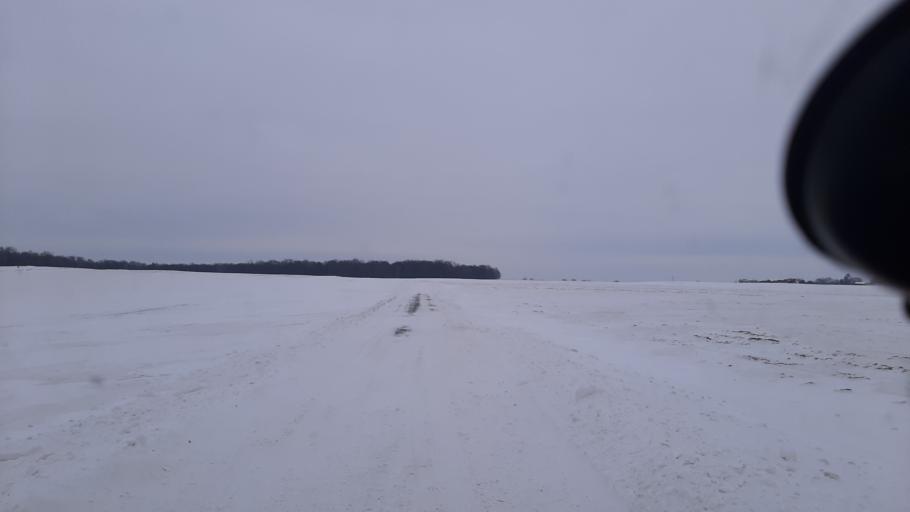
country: PL
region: Lublin Voivodeship
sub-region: Powiat lubelski
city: Garbow
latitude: 51.3244
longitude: 22.3093
